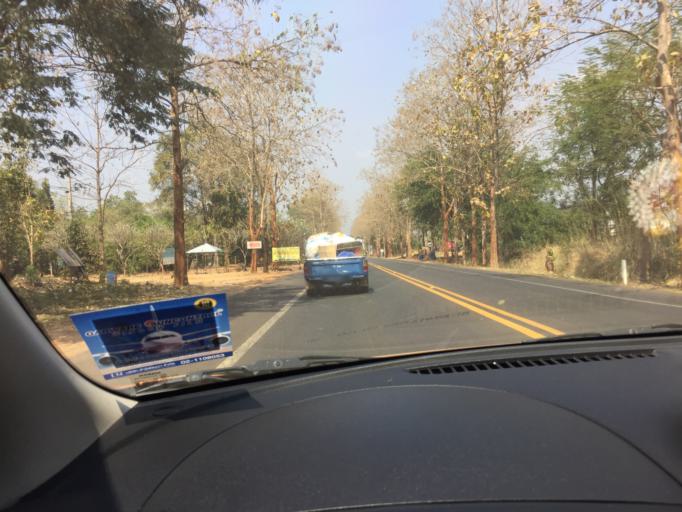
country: TH
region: Kanchanaburi
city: Sai Yok
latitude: 14.1760
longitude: 99.1280
